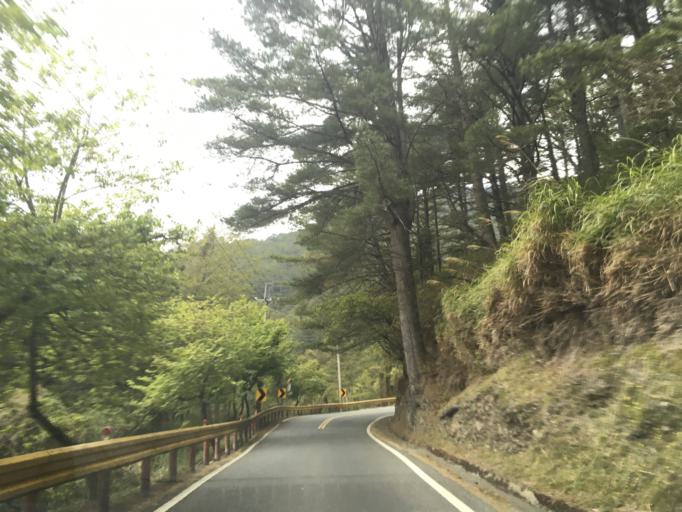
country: TW
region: Taiwan
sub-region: Hualien
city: Hualian
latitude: 24.1868
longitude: 121.3357
